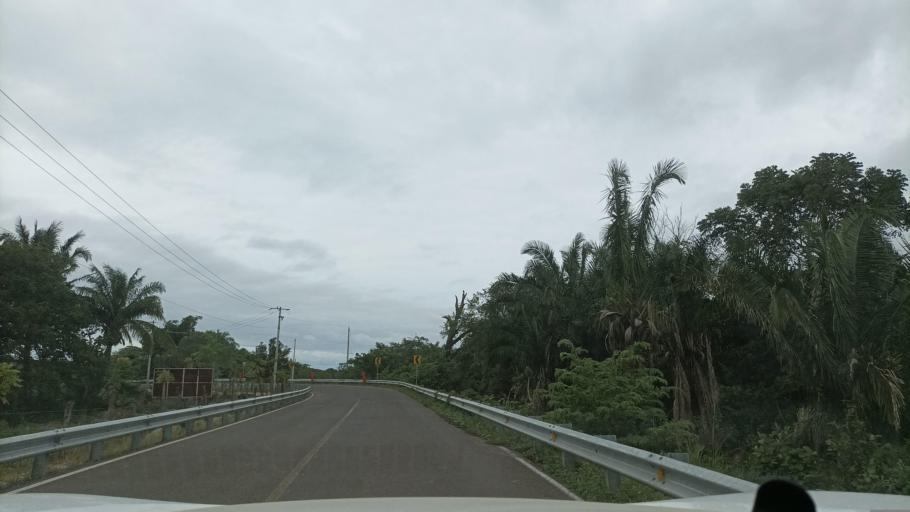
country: MX
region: Veracruz
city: Hidalgotitlan
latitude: 17.8113
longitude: -94.5627
